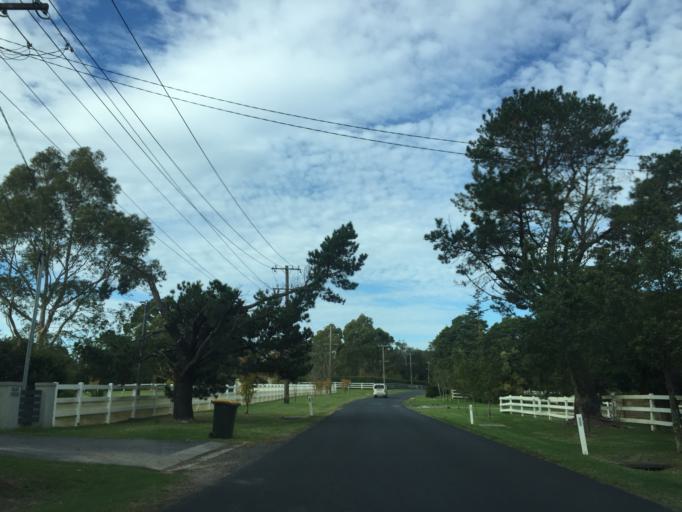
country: AU
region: New South Wales
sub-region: Hornsby Shire
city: Galston
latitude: -33.6470
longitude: 151.0727
